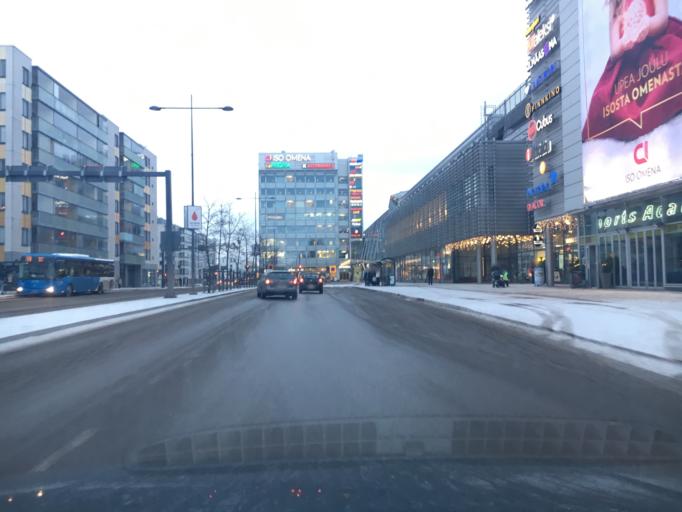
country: FI
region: Uusimaa
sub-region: Helsinki
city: Koukkuniemi
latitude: 60.1632
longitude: 24.7379
